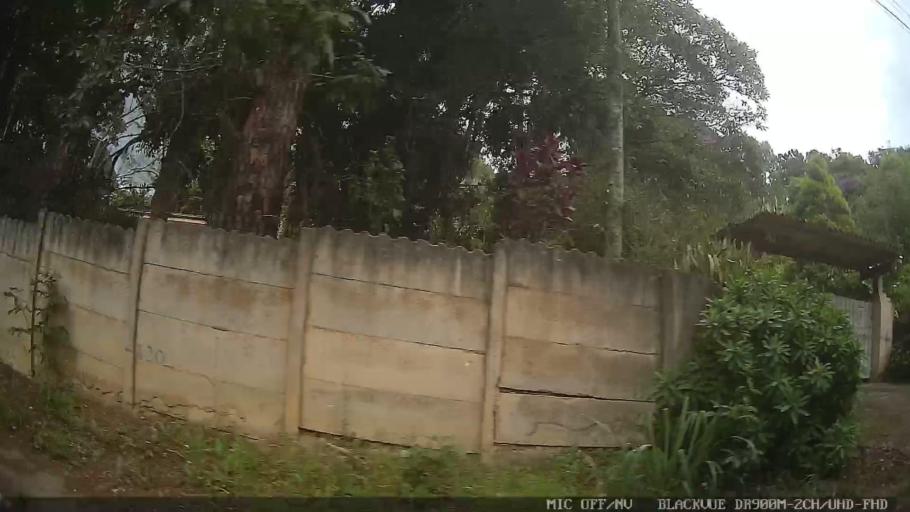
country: BR
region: Sao Paulo
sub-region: Atibaia
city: Atibaia
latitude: -23.1541
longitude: -46.5838
